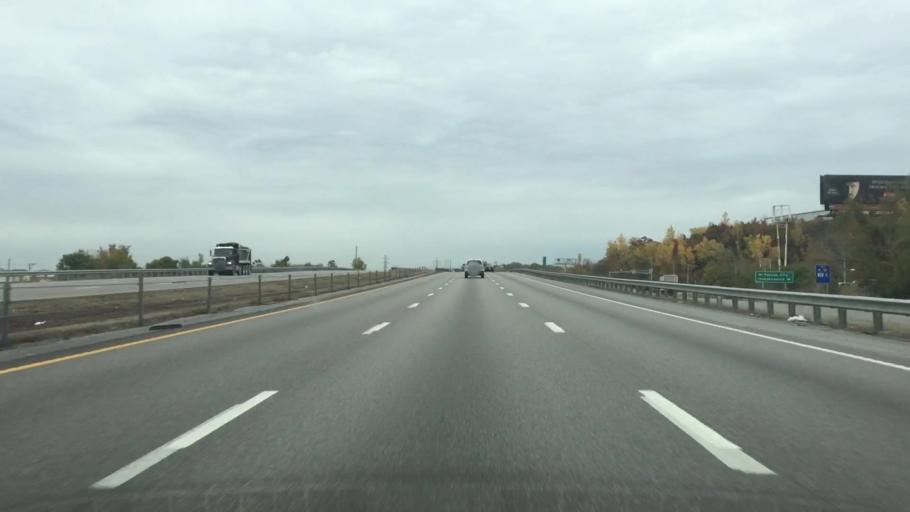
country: US
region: Missouri
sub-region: Jackson County
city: Sugar Creek
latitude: 39.0906
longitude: -94.4873
